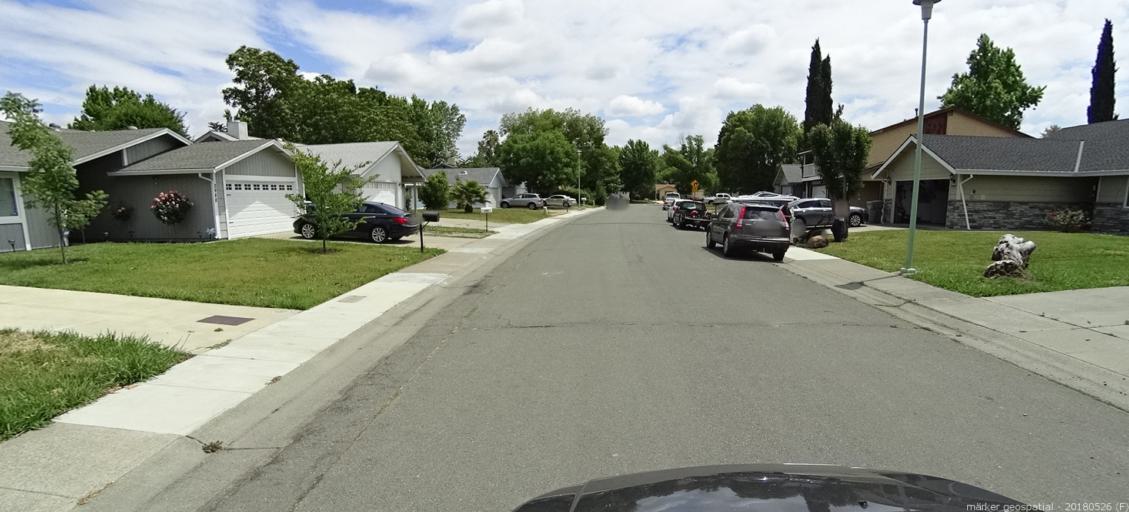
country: US
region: California
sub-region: Sacramento County
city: Sacramento
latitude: 38.6221
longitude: -121.4927
